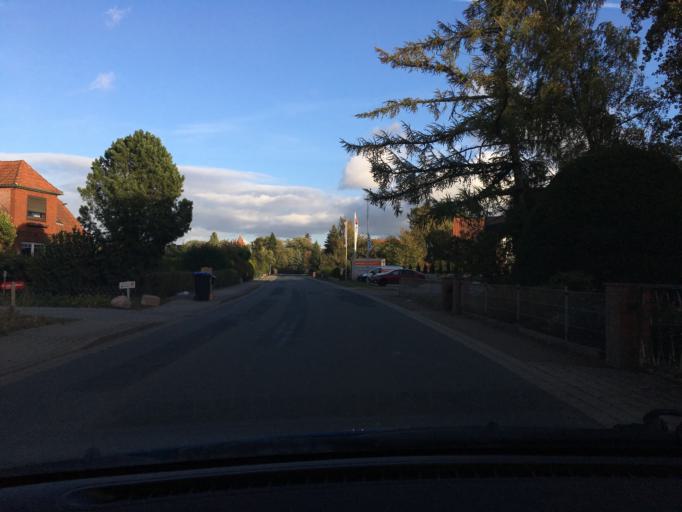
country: DE
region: Lower Saxony
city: Hittbergen
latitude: 53.3447
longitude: 10.5838
